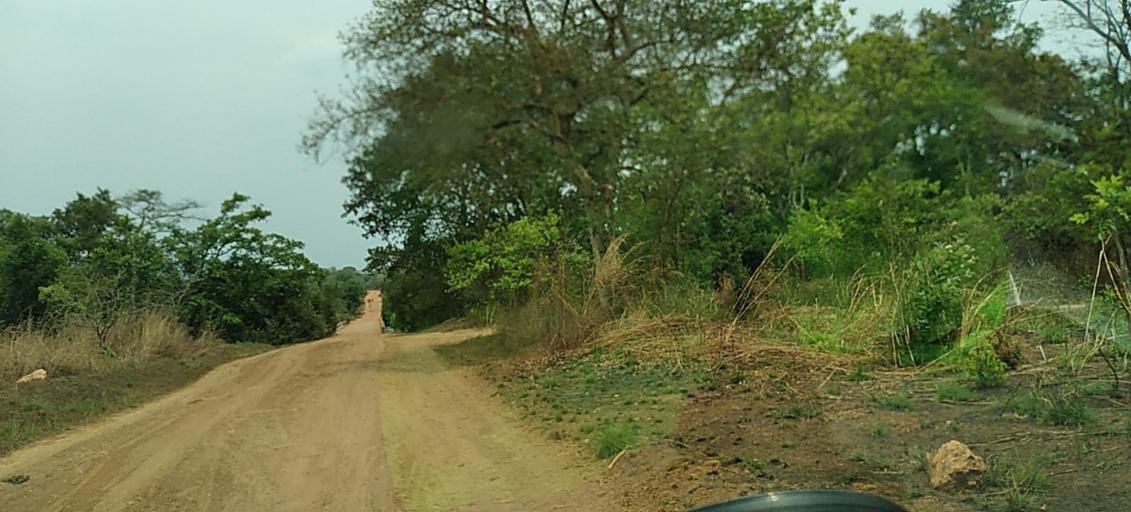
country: ZM
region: North-Western
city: Solwezi
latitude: -12.7952
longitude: 26.5325
